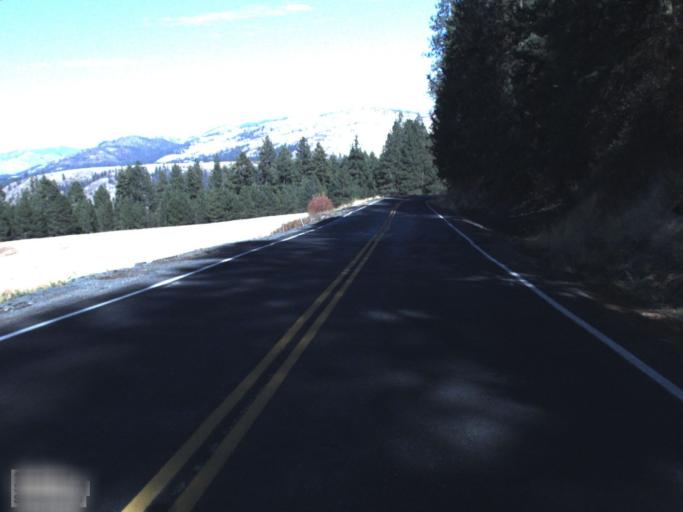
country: US
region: Washington
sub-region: Lincoln County
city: Davenport
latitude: 48.1339
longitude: -118.2029
